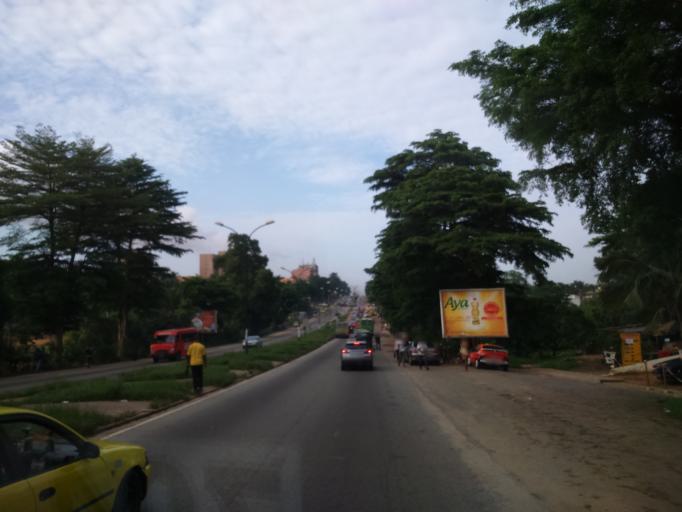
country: CI
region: Lagunes
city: Abidjan
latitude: 5.3514
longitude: -4.0022
